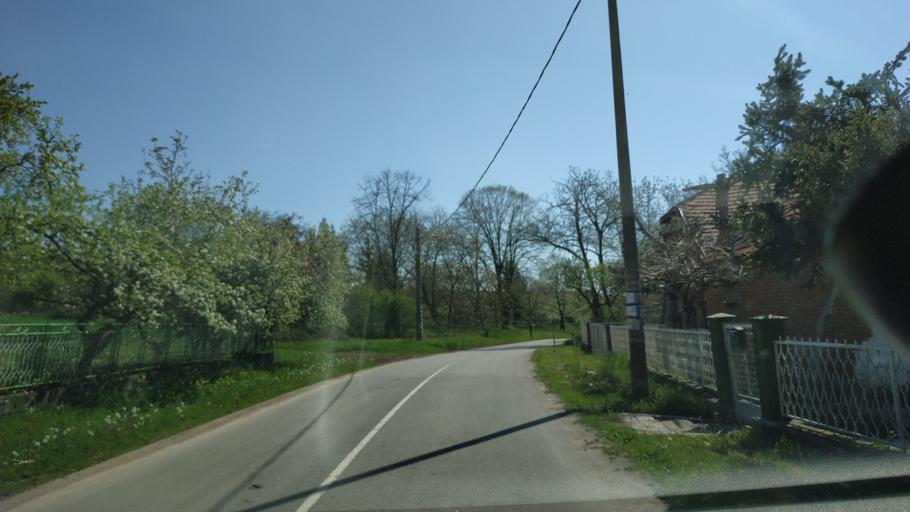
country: RS
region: Central Serbia
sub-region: Nisavski Okrug
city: Nis
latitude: 43.4623
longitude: 21.8610
